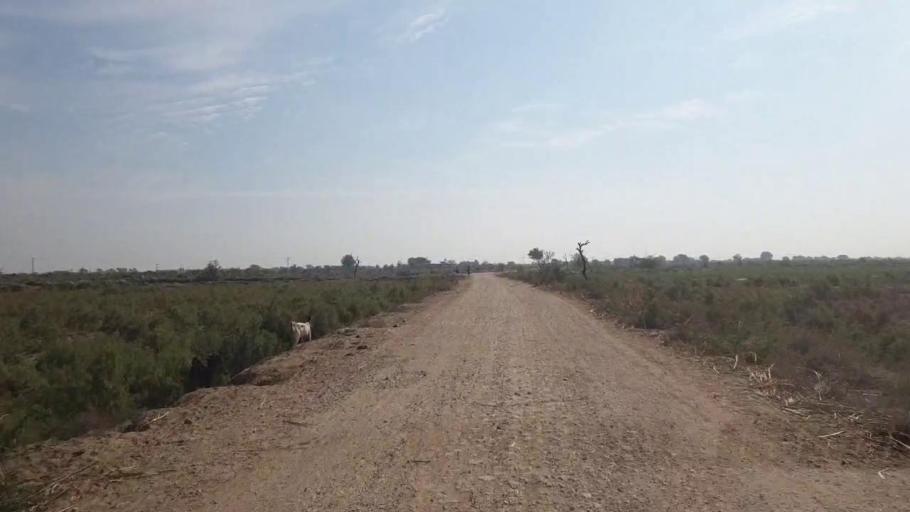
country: PK
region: Sindh
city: Mirwah Gorchani
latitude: 25.3671
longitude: 69.1885
